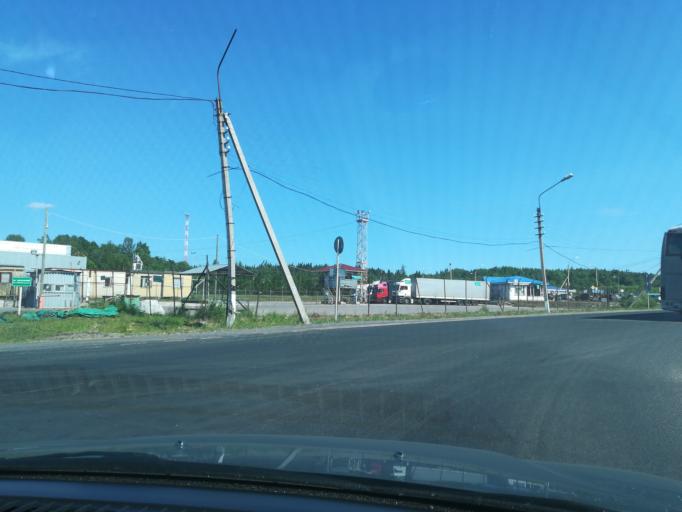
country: RU
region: Leningrad
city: Svetogorsk
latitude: 61.1192
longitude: 28.8478
